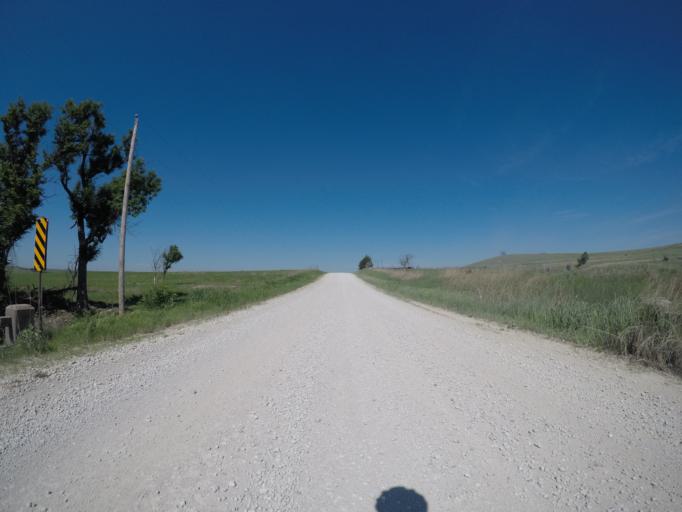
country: US
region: Kansas
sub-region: Wabaunsee County
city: Alma
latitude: 39.0154
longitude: -96.1207
